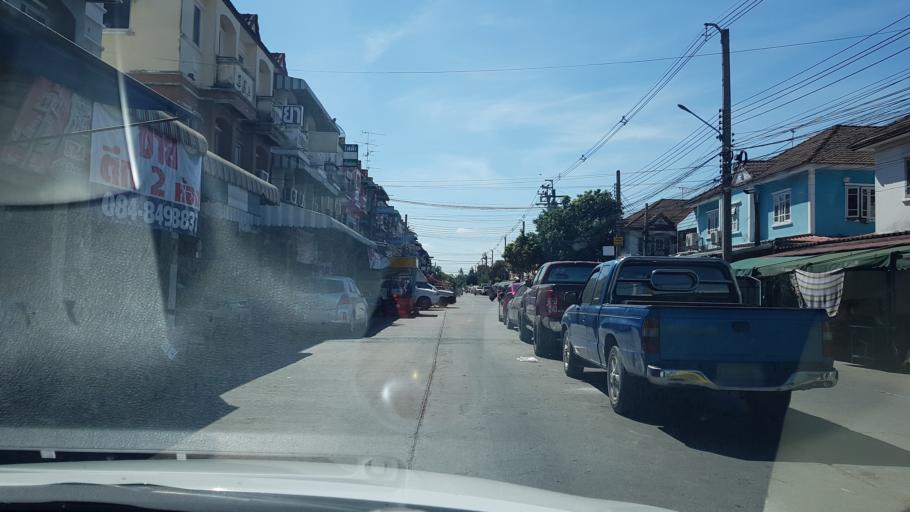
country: TH
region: Bangkok
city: Khlong Sam Wa
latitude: 13.8864
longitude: 100.7172
